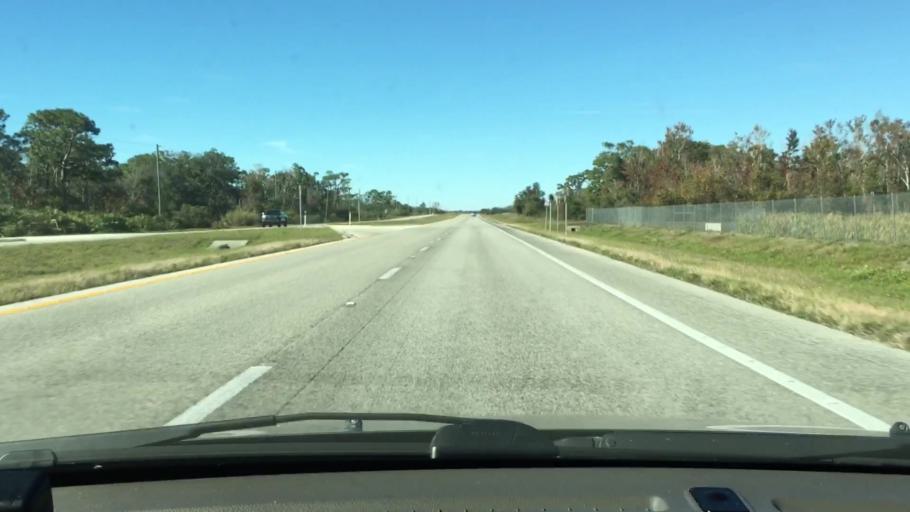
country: US
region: Florida
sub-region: Brevard County
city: June Park
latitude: 28.1251
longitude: -80.9695
